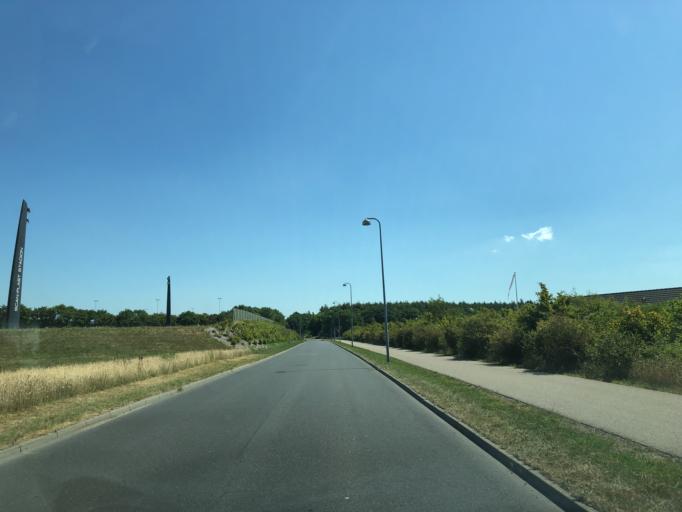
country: DK
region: Central Jutland
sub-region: Holstebro Kommune
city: Holstebro
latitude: 56.3613
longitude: 8.6798
